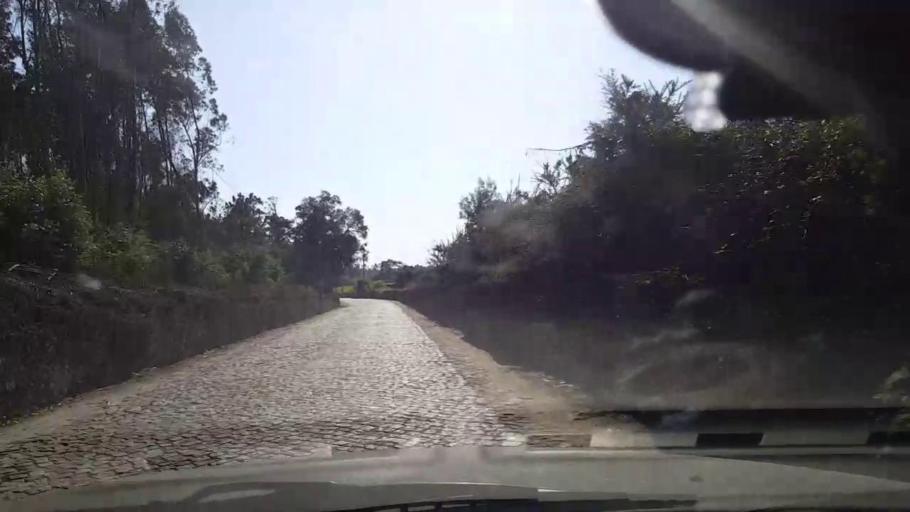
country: PT
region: Porto
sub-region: Vila do Conde
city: Arvore
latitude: 41.3540
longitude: -8.7036
